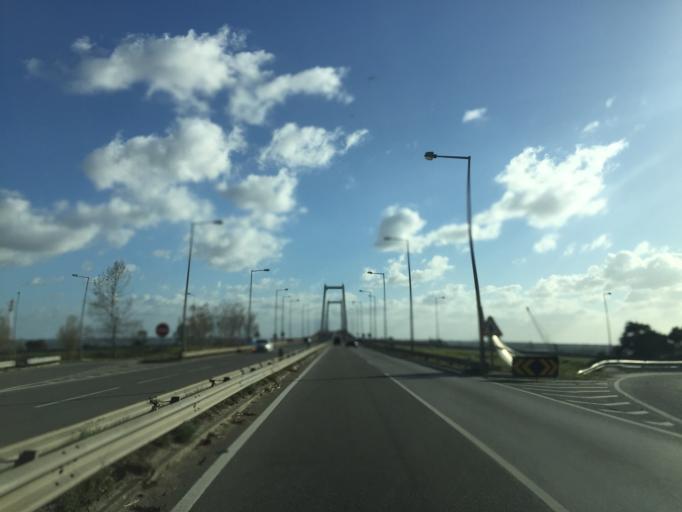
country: PT
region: Coimbra
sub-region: Figueira da Foz
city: Tavarede
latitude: 40.1516
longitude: -8.8417
